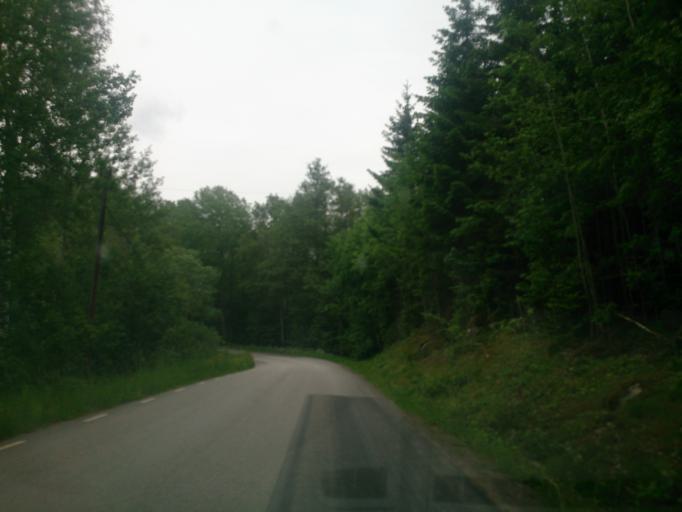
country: SE
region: OEstergoetland
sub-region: Atvidabergs Kommun
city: Atvidaberg
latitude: 58.2778
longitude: 16.1657
